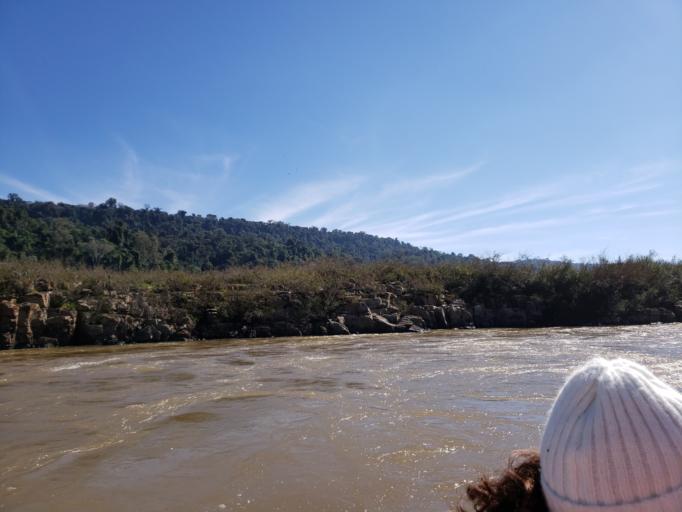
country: BR
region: Rio Grande do Sul
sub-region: Tres Passos
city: Tres Passos
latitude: -27.1522
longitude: -53.8881
